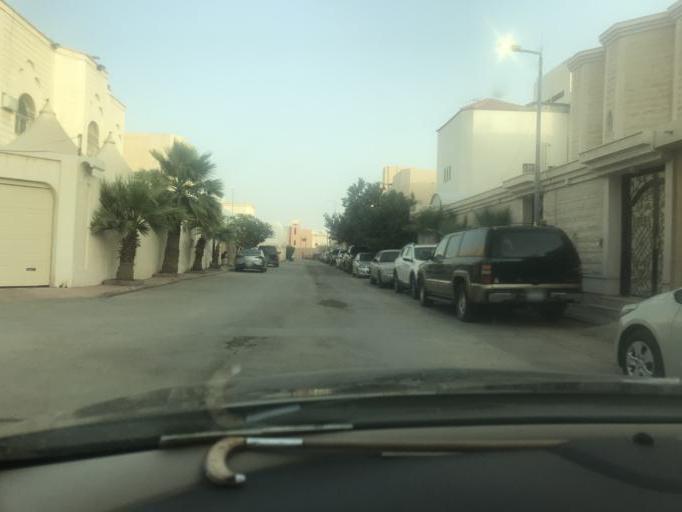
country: SA
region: Ar Riyad
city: Riyadh
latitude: 24.7455
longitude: 46.7792
